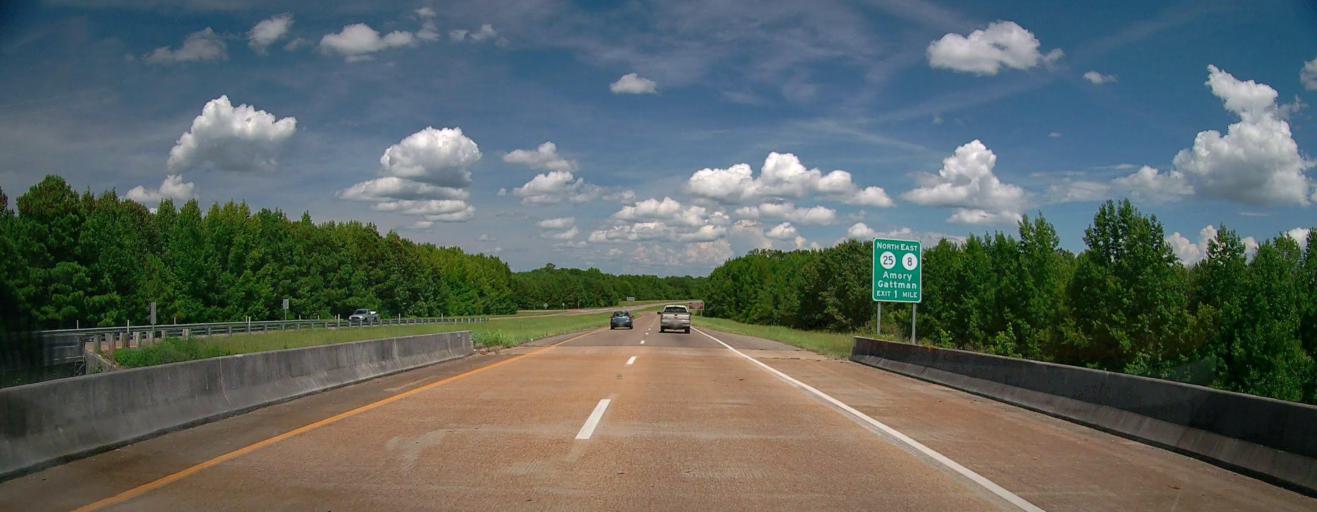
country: US
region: Mississippi
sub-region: Monroe County
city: Aberdeen
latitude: 33.8186
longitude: -88.5138
